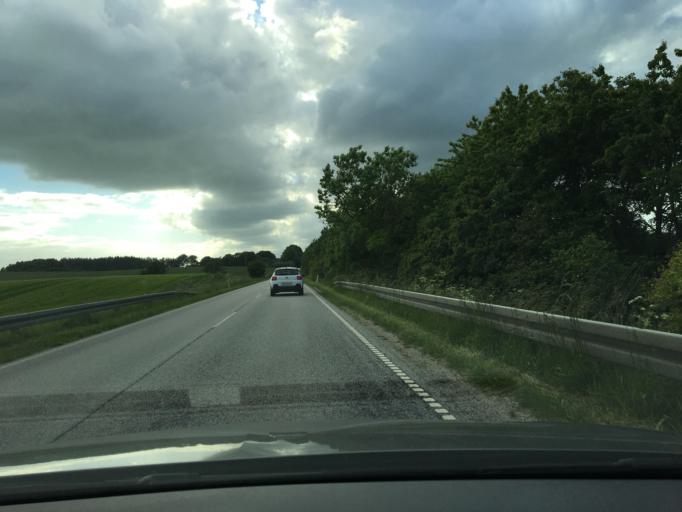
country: DK
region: Central Jutland
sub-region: Arhus Kommune
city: Logten
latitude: 56.2898
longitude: 10.3025
